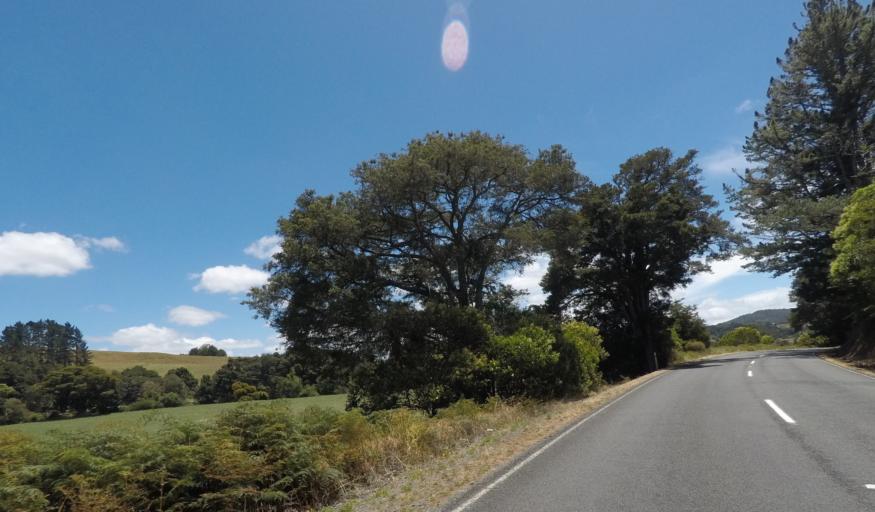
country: NZ
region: Northland
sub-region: Whangarei
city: Whangarei
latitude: -35.5387
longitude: 174.3100
